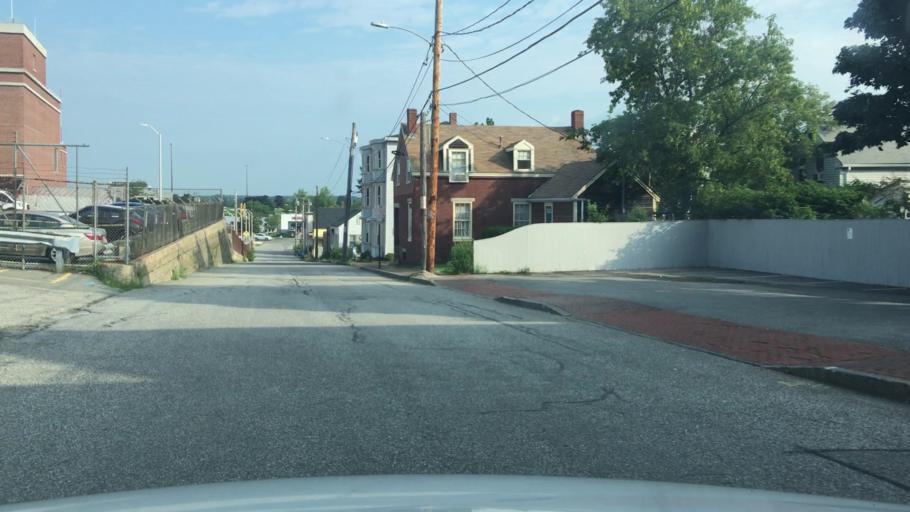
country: US
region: Maine
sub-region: Cumberland County
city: Portland
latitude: 43.6581
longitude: -70.2651
